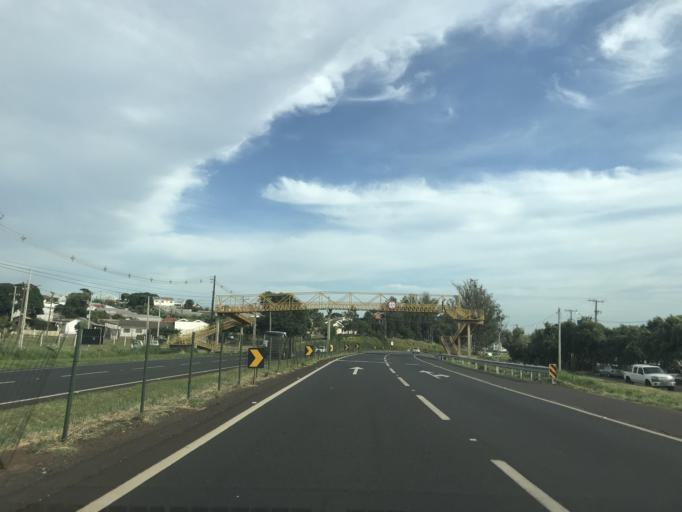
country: BR
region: Parana
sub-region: Mandaguacu
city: Mandaguacu
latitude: -23.3547
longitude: -52.0905
